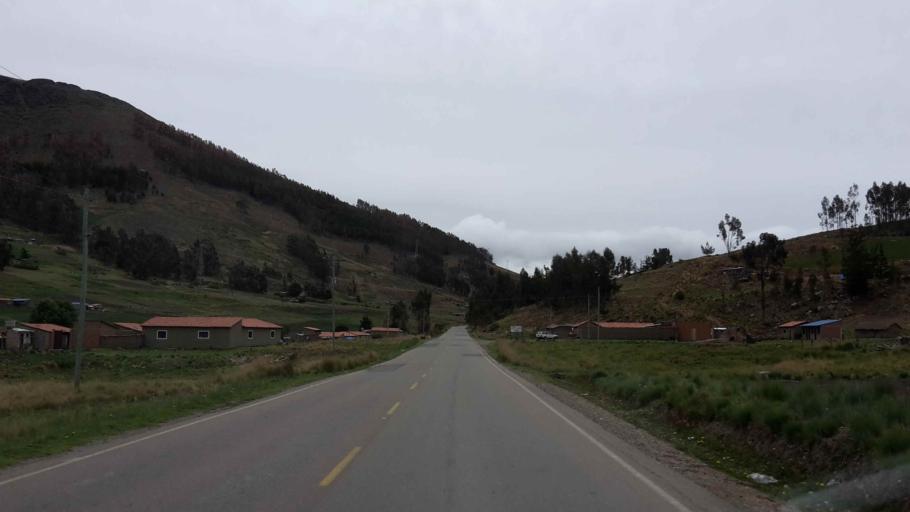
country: BO
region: Cochabamba
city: Arani
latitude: -17.4807
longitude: -65.5810
